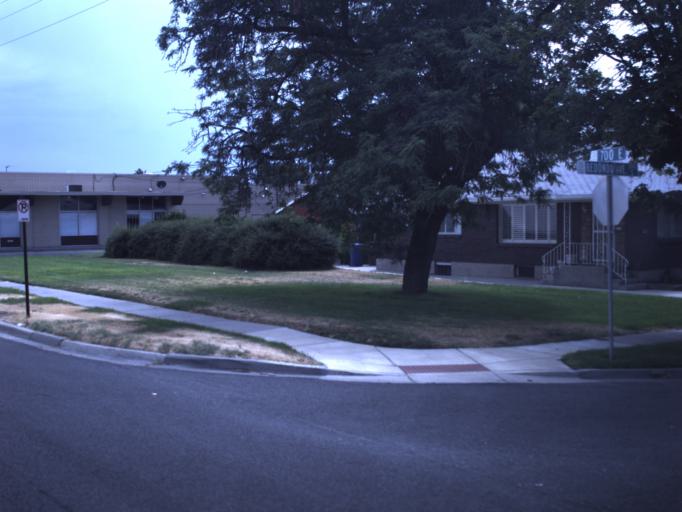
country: US
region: Utah
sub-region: Salt Lake County
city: South Salt Lake
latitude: 40.7268
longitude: -111.8713
